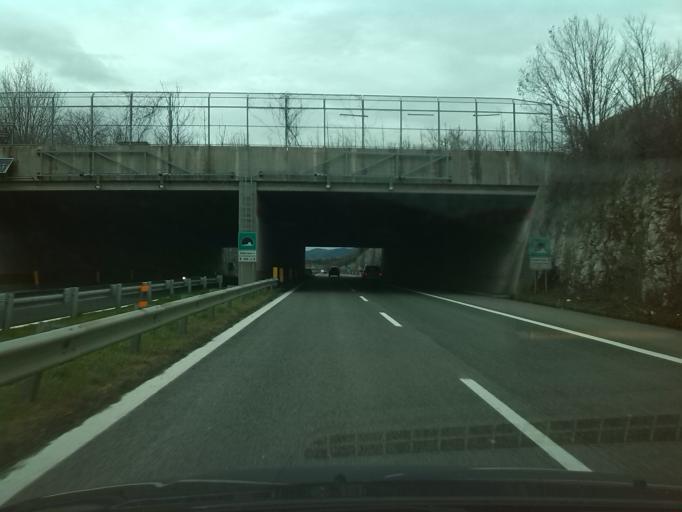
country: IT
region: Friuli Venezia Giulia
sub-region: Provincia di Trieste
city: Trieste
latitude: 45.6667
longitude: 13.8257
